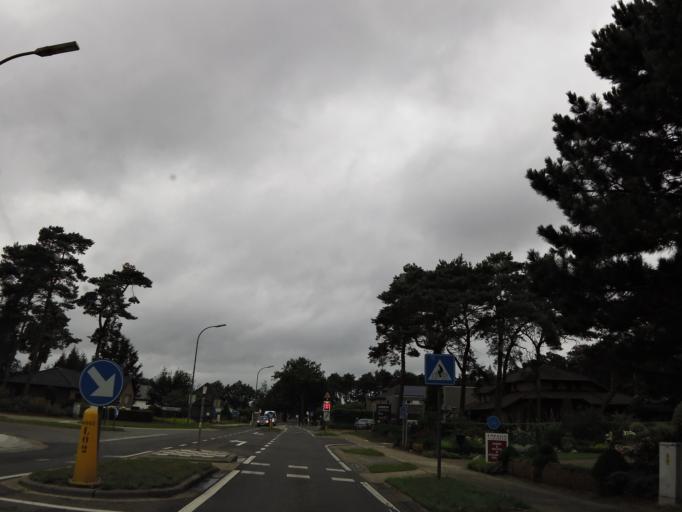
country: BE
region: Flanders
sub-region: Provincie Limburg
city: Bree
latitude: 51.1207
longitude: 5.5920
